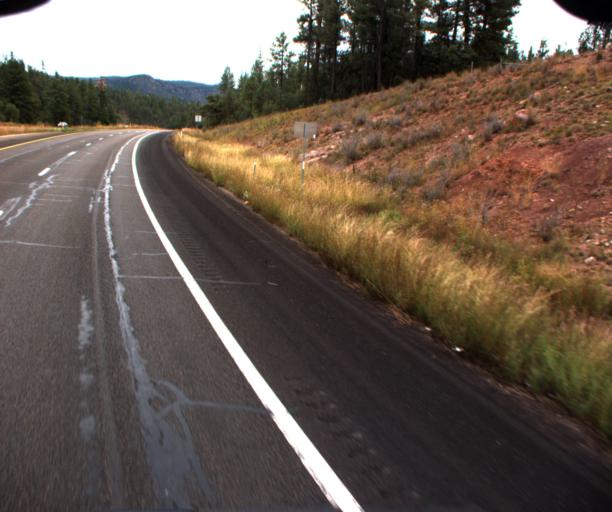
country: US
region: Arizona
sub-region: Gila County
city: Star Valley
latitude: 34.3284
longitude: -111.0891
